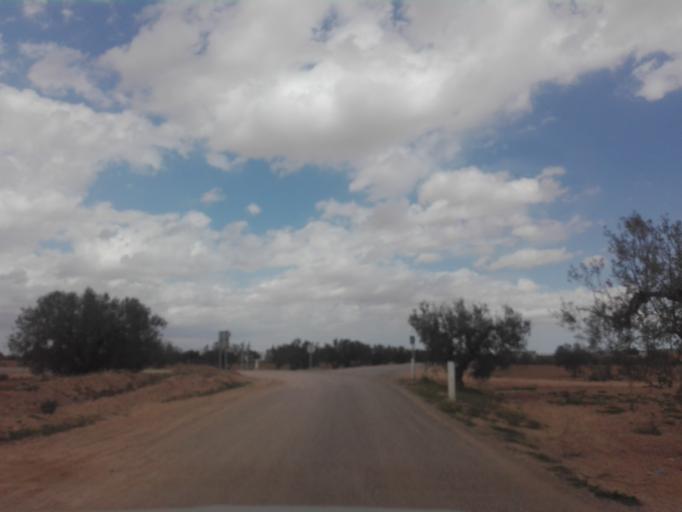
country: TN
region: Safaqis
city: Sfax
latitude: 34.6869
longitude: 10.4432
